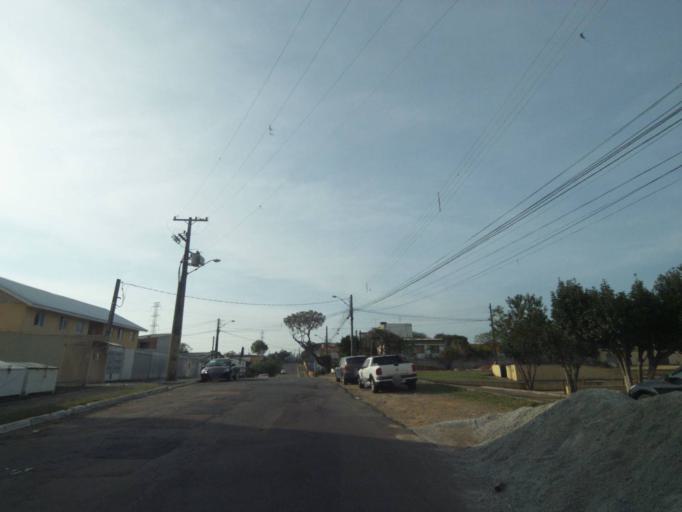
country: BR
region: Parana
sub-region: Curitiba
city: Curitiba
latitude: -25.4651
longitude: -49.3123
